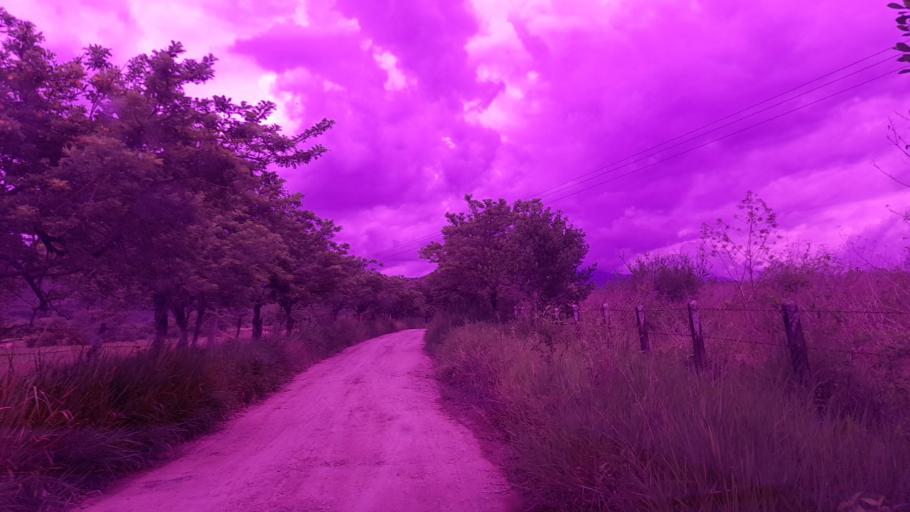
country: CO
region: Valle del Cauca
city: Andalucia
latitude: 4.1782
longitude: -76.1328
